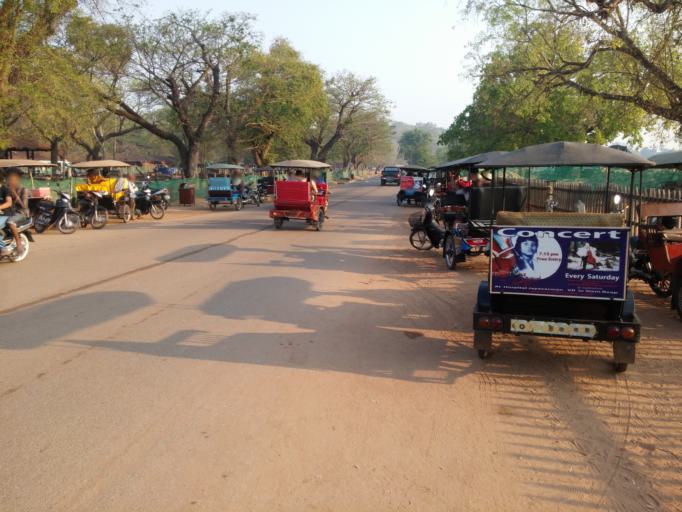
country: KH
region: Siem Reap
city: Siem Reap
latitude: 13.4125
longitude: 103.8595
